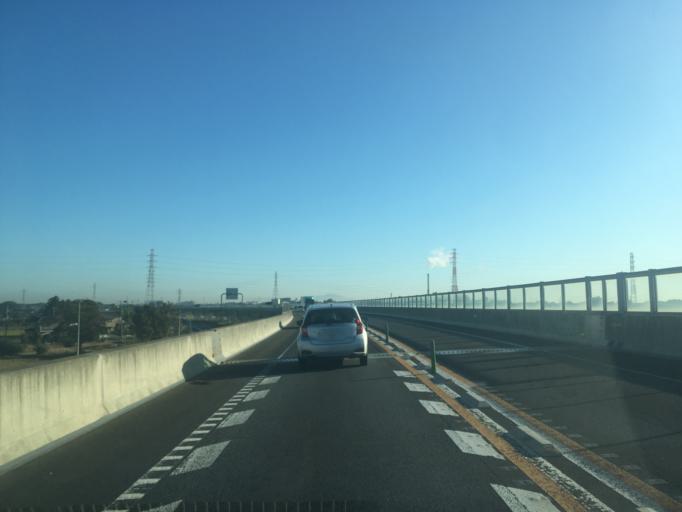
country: JP
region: Saitama
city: Kukichuo
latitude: 36.0456
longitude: 139.6799
